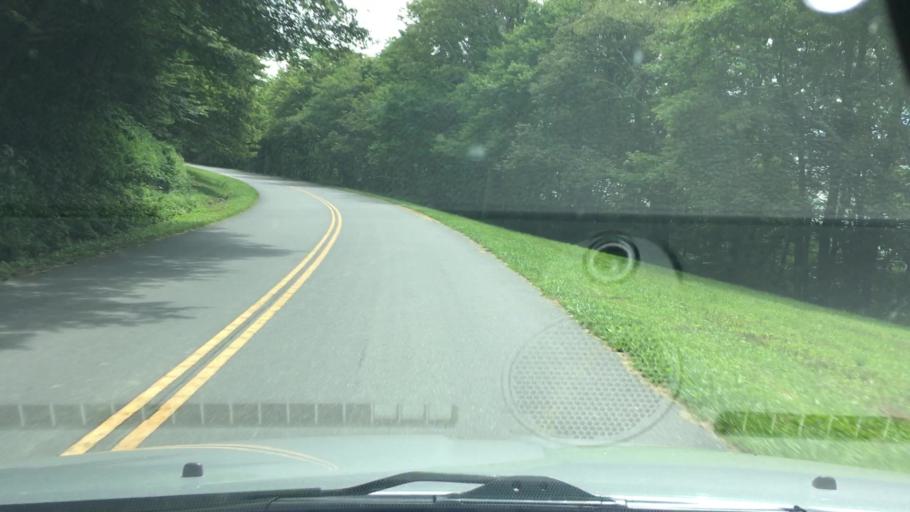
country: US
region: North Carolina
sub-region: Buncombe County
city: Swannanoa
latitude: 35.6925
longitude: -82.3907
